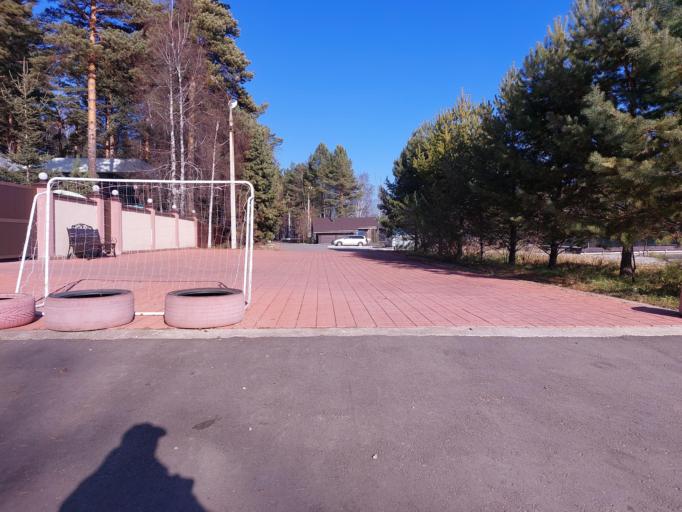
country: RU
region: Irkutsk
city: Pivovarikha
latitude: 52.1873
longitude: 104.4656
